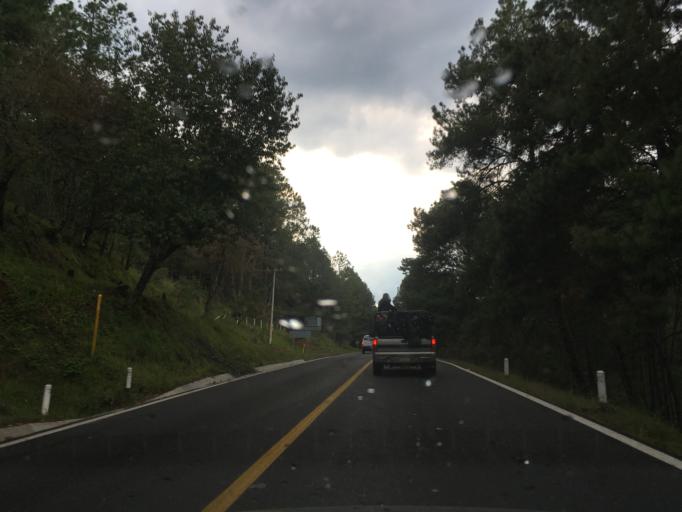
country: MX
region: Michoacan
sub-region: Patzcuaro
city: Santa Maria Huiramangaro (San Juan Tumbio)
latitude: 19.5002
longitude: -101.7540
